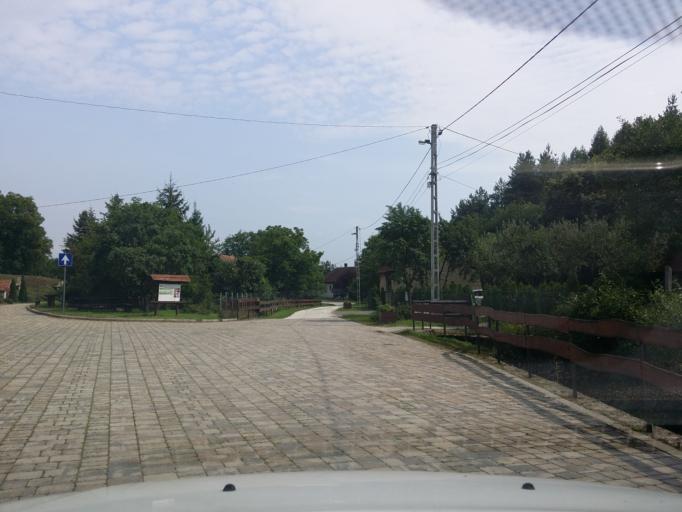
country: HU
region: Borsod-Abauj-Zemplen
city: Satoraljaujhely
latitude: 48.4587
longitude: 21.5859
